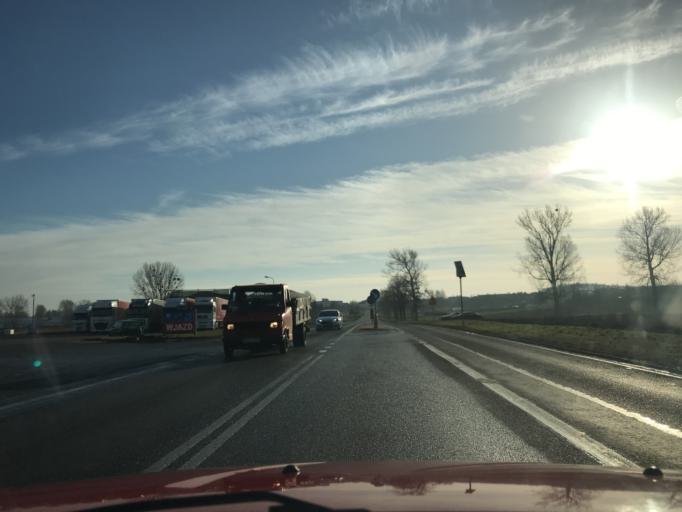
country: PL
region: Greater Poland Voivodeship
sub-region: Powiat jarocinski
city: Kotlin
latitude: 51.9241
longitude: 17.6362
